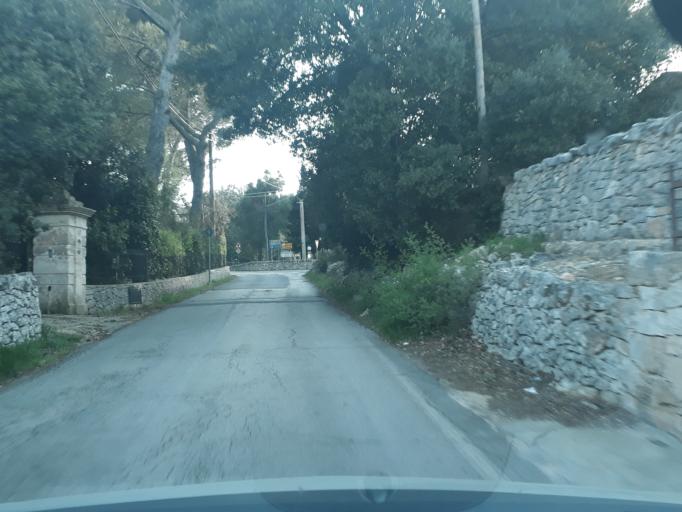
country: IT
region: Apulia
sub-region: Provincia di Brindisi
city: Lamie di Olimpie-Selva
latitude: 40.8271
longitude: 17.3312
